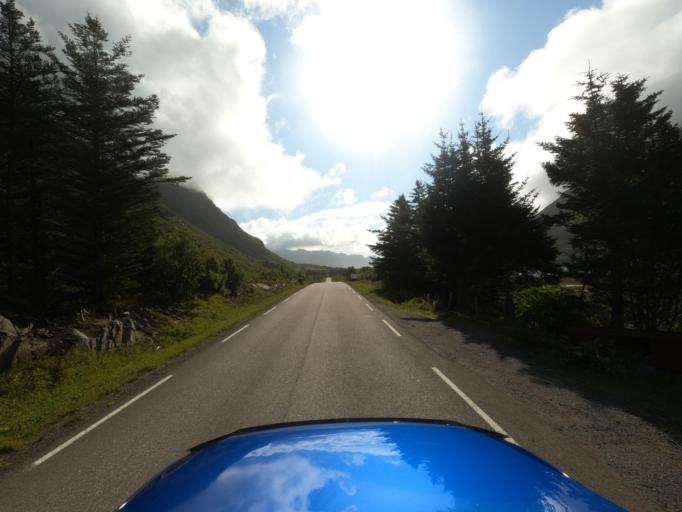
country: NO
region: Nordland
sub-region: Vagan
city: Kabelvag
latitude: 68.2774
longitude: 14.1618
